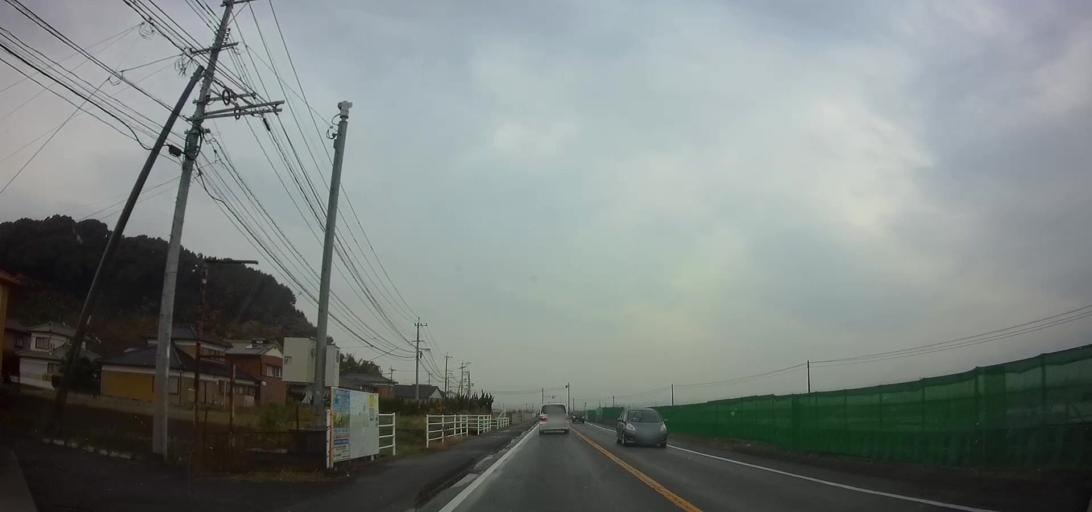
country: JP
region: Nagasaki
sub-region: Isahaya-shi
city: Isahaya
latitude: 32.8369
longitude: 130.1057
